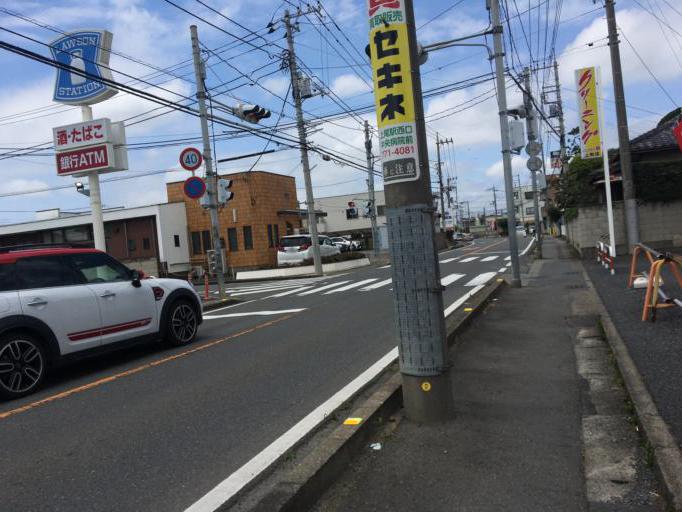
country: JP
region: Saitama
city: Ageoshimo
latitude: 35.9786
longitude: 139.5855
